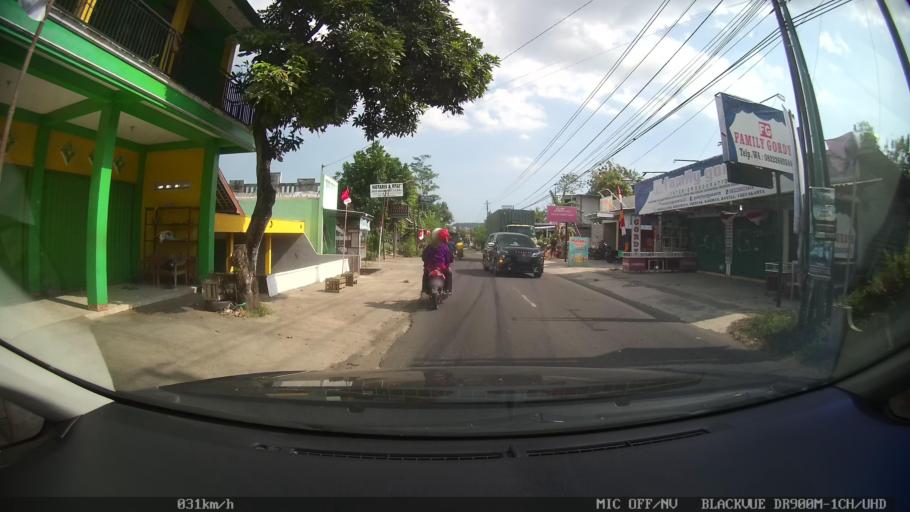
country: ID
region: Daerah Istimewa Yogyakarta
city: Kasihan
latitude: -7.8339
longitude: 110.3135
